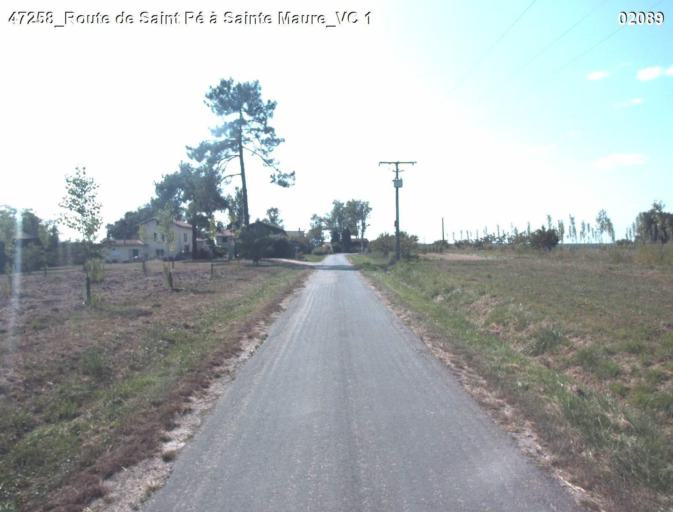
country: FR
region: Midi-Pyrenees
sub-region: Departement du Gers
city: Montreal
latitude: 44.0133
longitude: 0.1450
